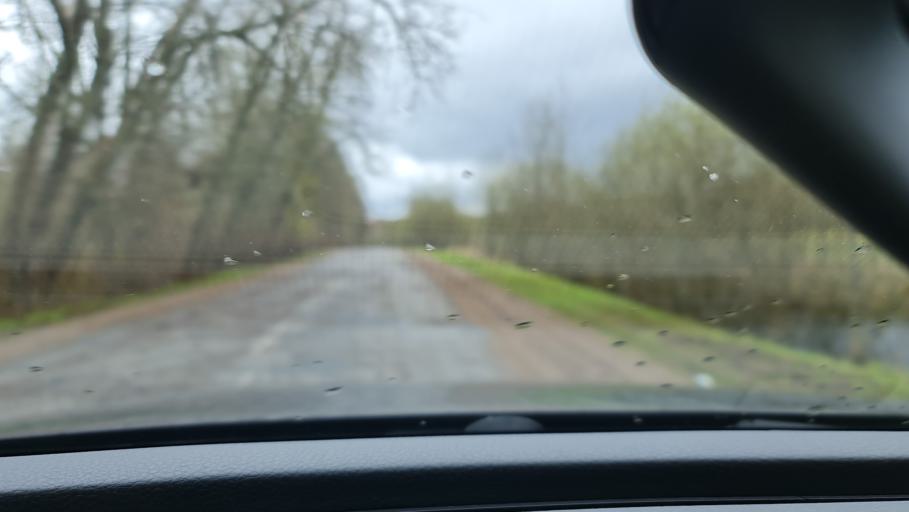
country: RU
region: Novgorod
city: Marevo
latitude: 57.2847
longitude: 32.0798
